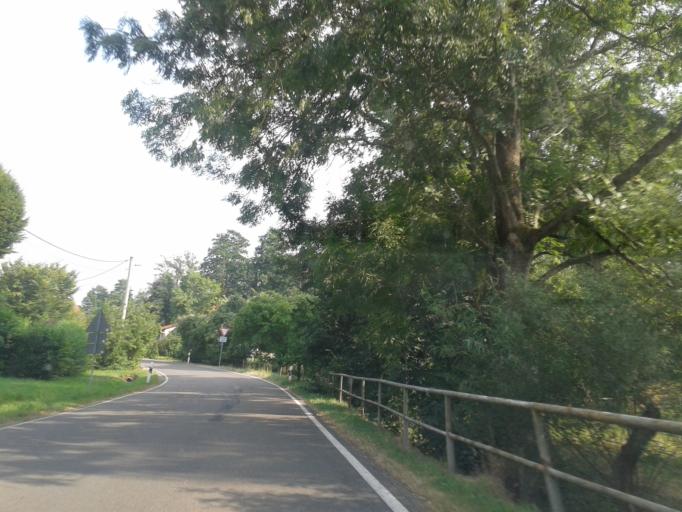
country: DE
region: Saxony
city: Reinsberg
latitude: 51.0036
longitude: 13.3849
